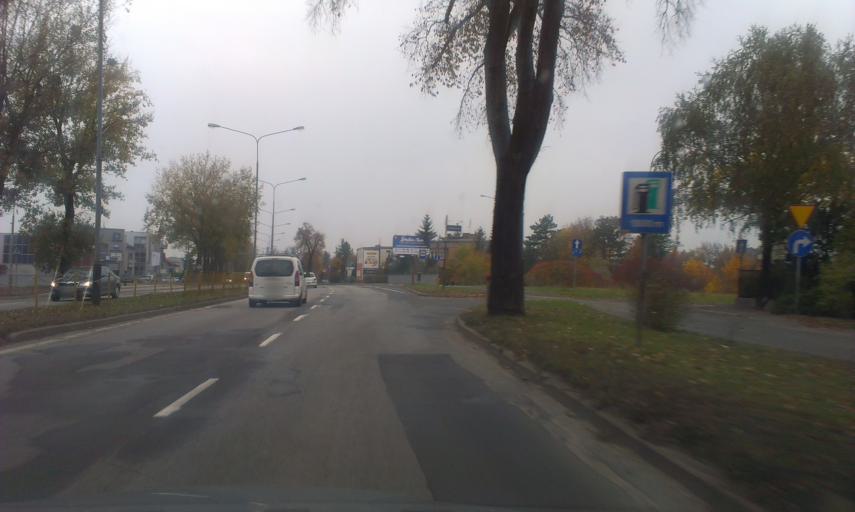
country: PL
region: Greater Poland Voivodeship
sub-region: Powiat poznanski
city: Suchy Las
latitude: 52.4259
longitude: 16.8608
